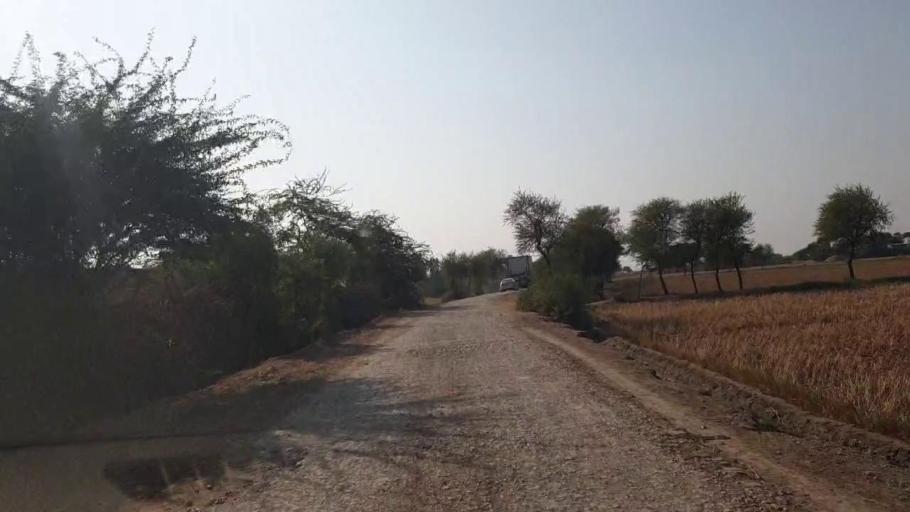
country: PK
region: Sindh
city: Matli
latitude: 24.9514
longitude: 68.6883
